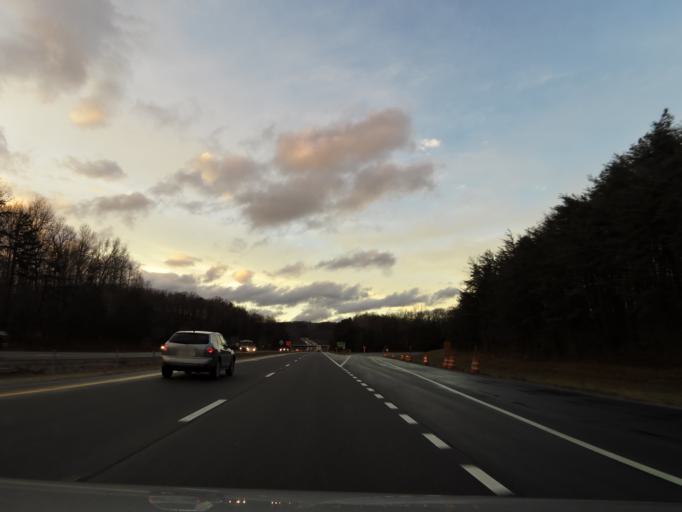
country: US
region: Tennessee
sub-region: Campbell County
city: Jacksboro
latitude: 36.4123
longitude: -84.2791
